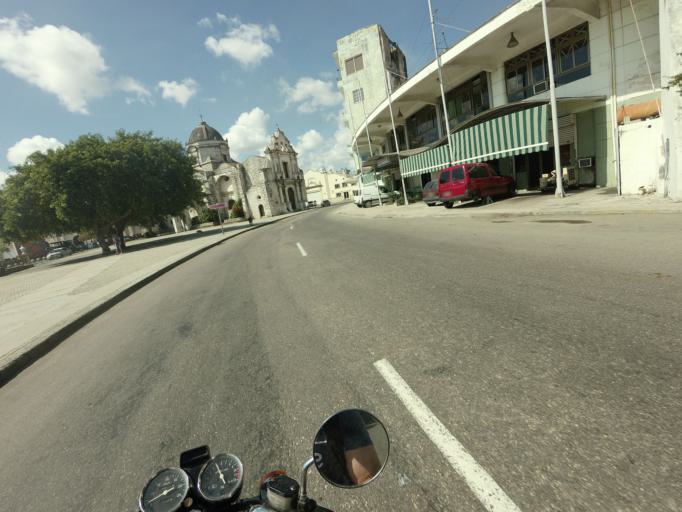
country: TM
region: Balkan
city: Gumdag
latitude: 38.8430
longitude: 54.1883
